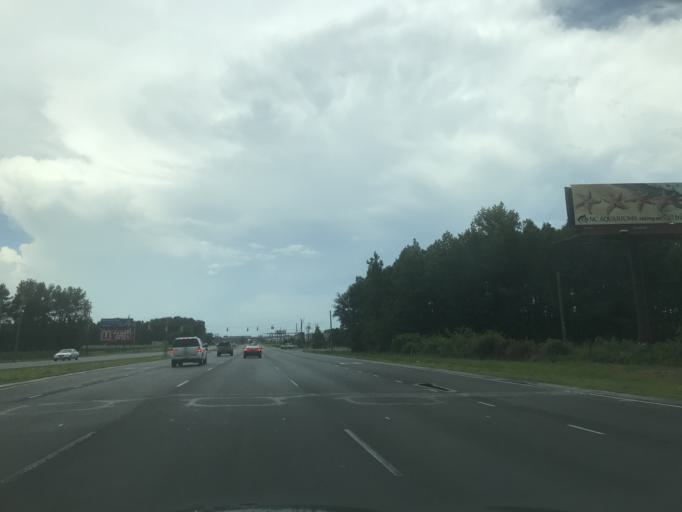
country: US
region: North Carolina
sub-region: Johnston County
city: Clayton
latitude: 35.6073
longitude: -78.4162
